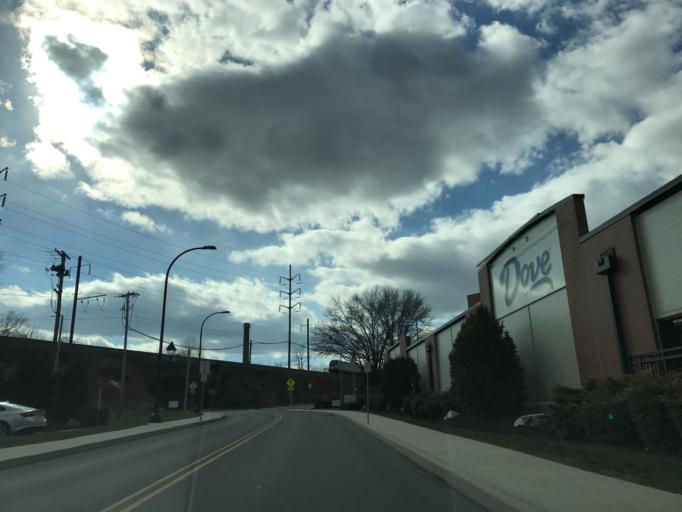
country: US
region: Pennsylvania
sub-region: Lancaster County
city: Elizabethtown
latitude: 40.1458
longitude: -76.6063
